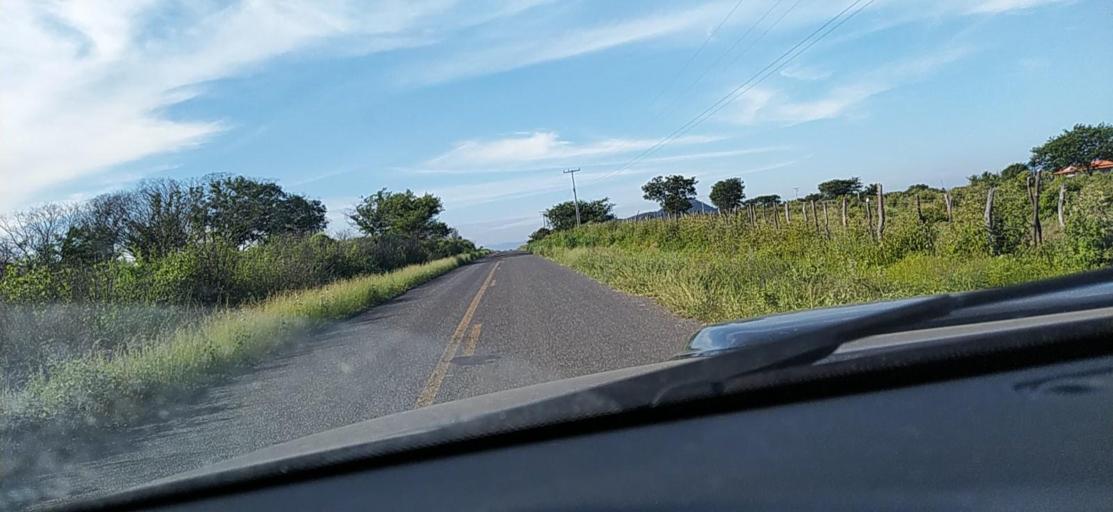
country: BR
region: Bahia
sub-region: Guanambi
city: Guanambi
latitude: -14.0078
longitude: -42.8585
